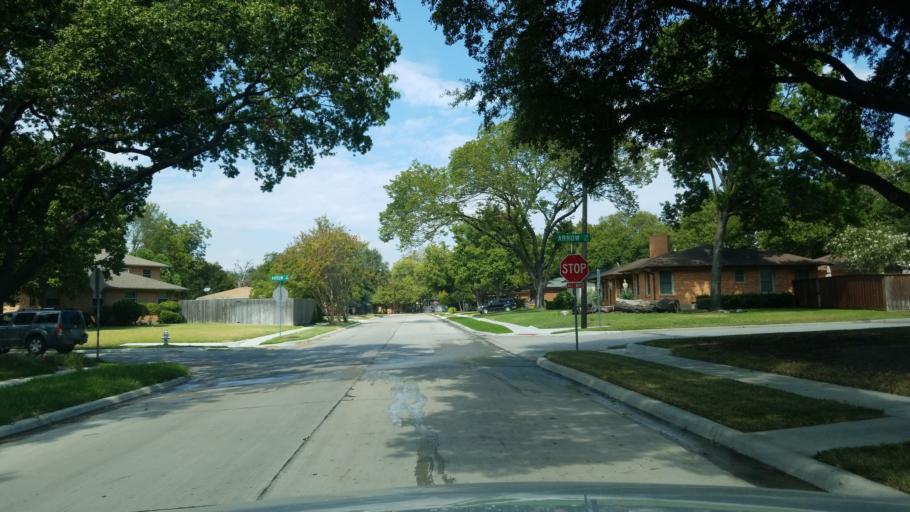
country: US
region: Texas
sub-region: Dallas County
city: Garland
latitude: 32.8960
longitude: -96.6578
